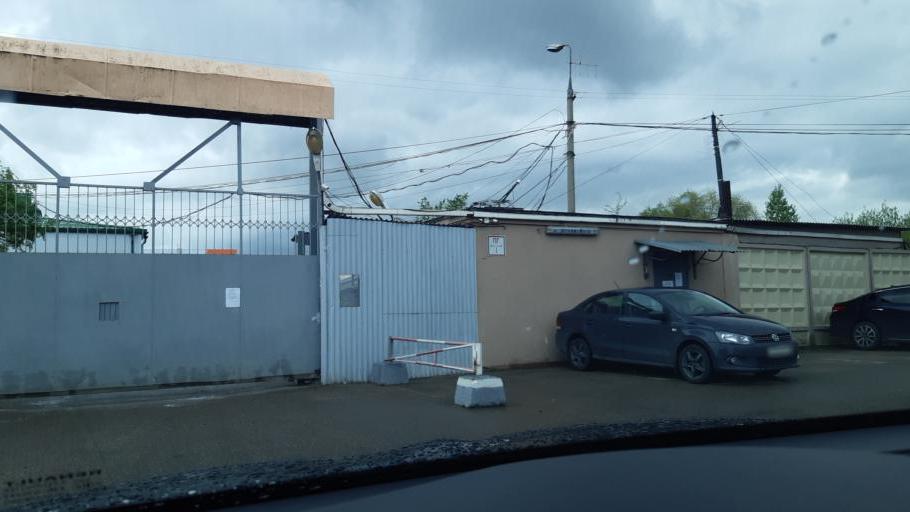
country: RU
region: Moskovskaya
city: Dolgoprudnyy
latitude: 55.9231
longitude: 37.5043
